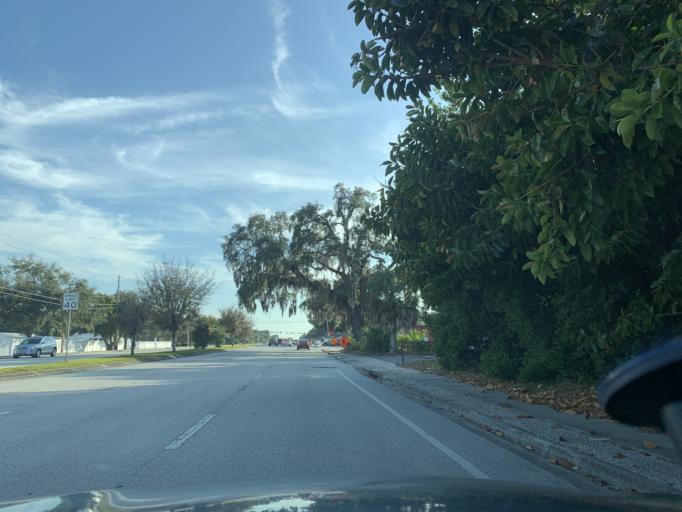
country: US
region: Florida
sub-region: Pinellas County
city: Ridgecrest
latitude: 27.8978
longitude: -82.7955
